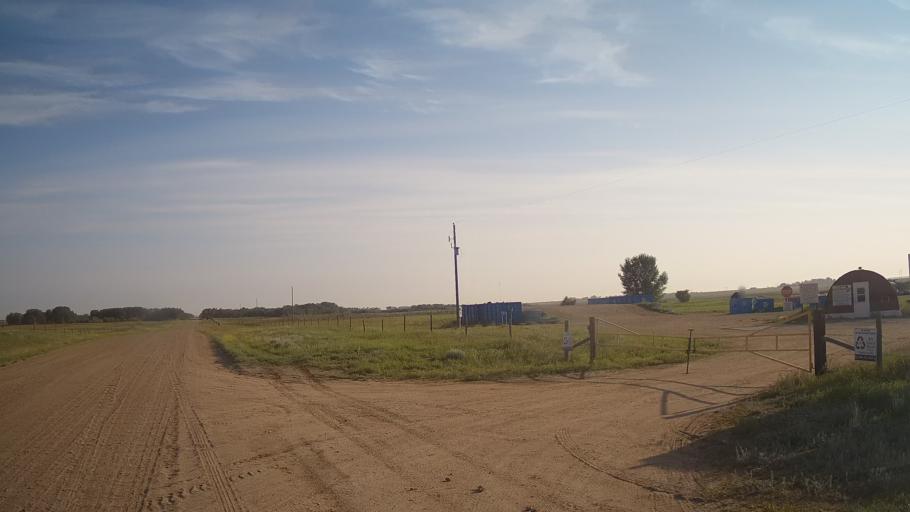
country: CA
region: Saskatchewan
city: Saskatoon
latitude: 51.8235
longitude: -106.5238
